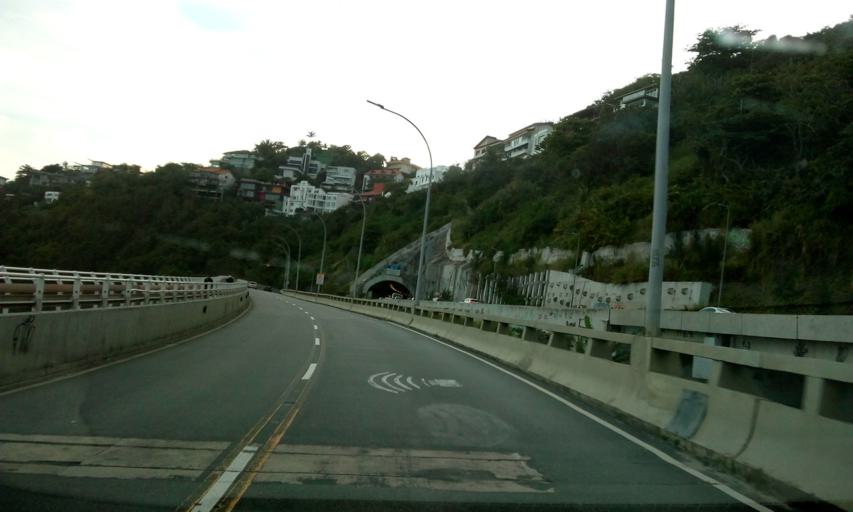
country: BR
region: Rio de Janeiro
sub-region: Rio De Janeiro
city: Rio de Janeiro
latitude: -23.0085
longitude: -43.2860
